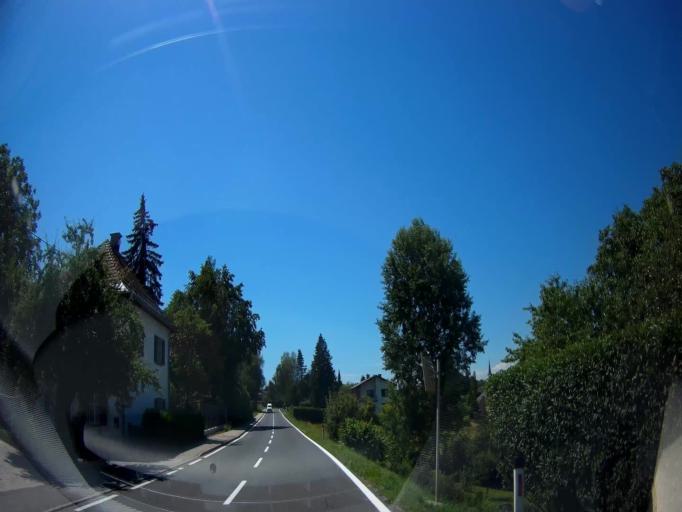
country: AT
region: Carinthia
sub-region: Politischer Bezirk Volkermarkt
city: Eberndorf
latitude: 46.6133
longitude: 14.5831
